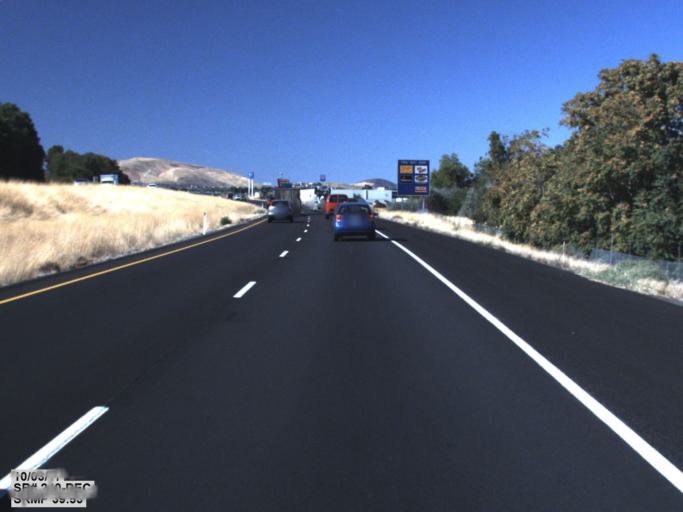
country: US
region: Washington
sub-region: Franklin County
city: West Pasco
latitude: 46.2320
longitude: -119.2102
